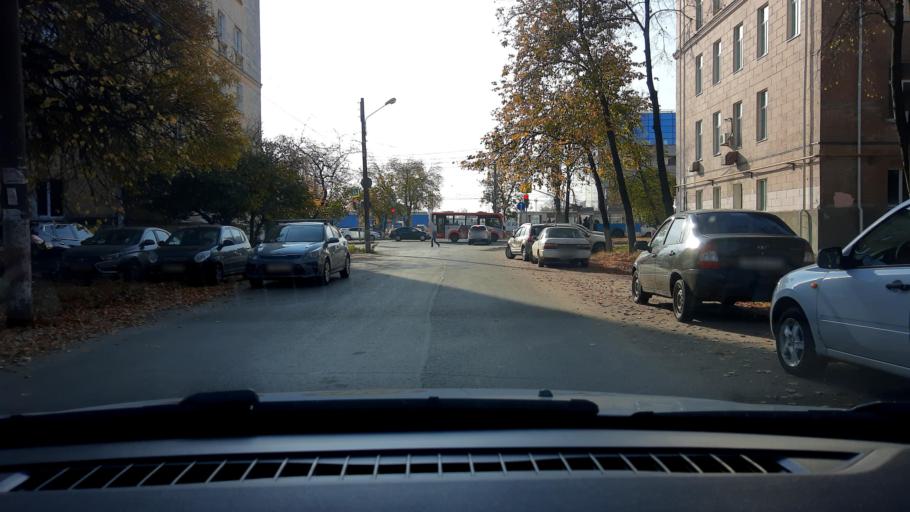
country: RU
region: Nizjnij Novgorod
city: Nizhniy Novgorod
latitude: 56.3185
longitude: 43.9186
